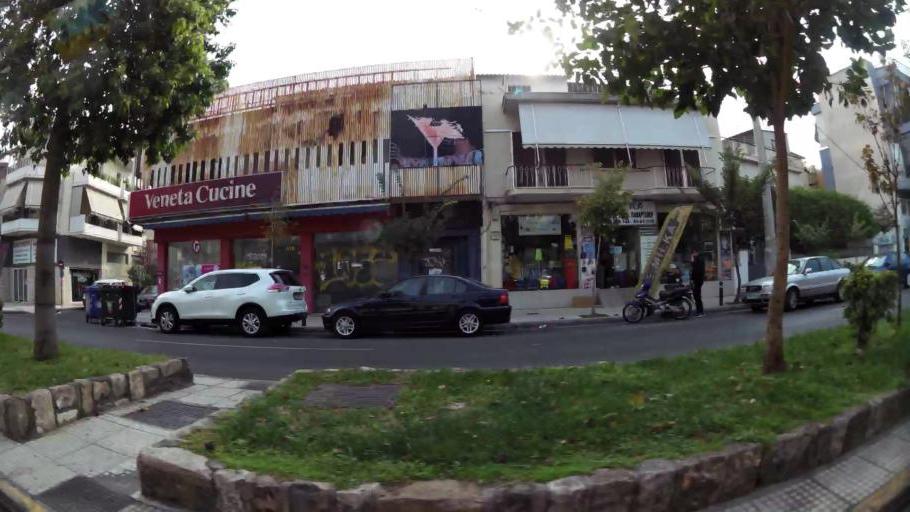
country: GR
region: Attica
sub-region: Nomarchia Athinas
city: Aigaleo
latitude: 37.9980
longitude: 23.6826
